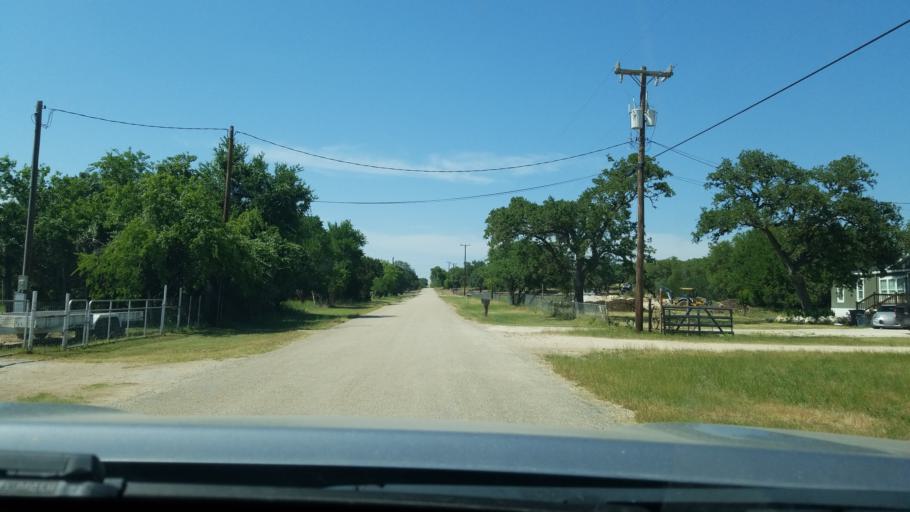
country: US
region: Texas
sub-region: Bexar County
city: Timberwood Park
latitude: 29.7518
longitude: -98.5153
